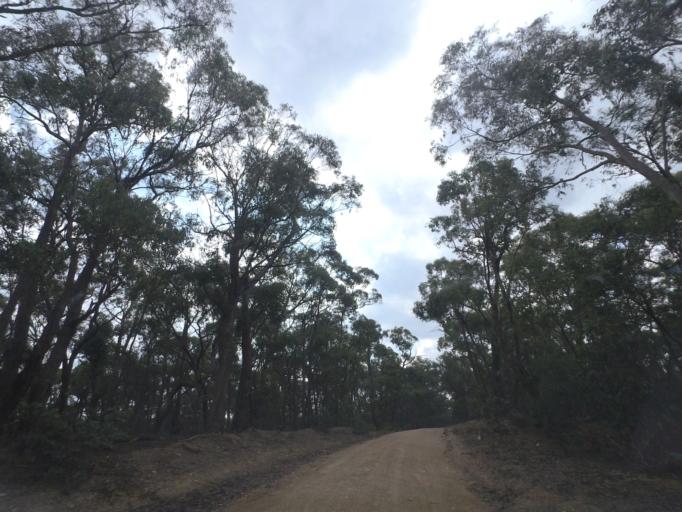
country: AU
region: Victoria
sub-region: Moorabool
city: Bacchus Marsh
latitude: -37.5099
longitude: 144.4299
